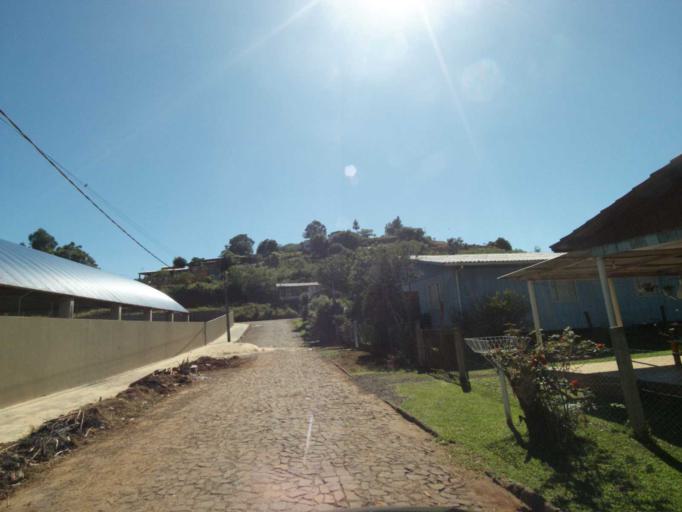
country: BR
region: Parana
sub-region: Francisco Beltrao
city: Francisco Beltrao
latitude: -26.1452
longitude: -53.3070
